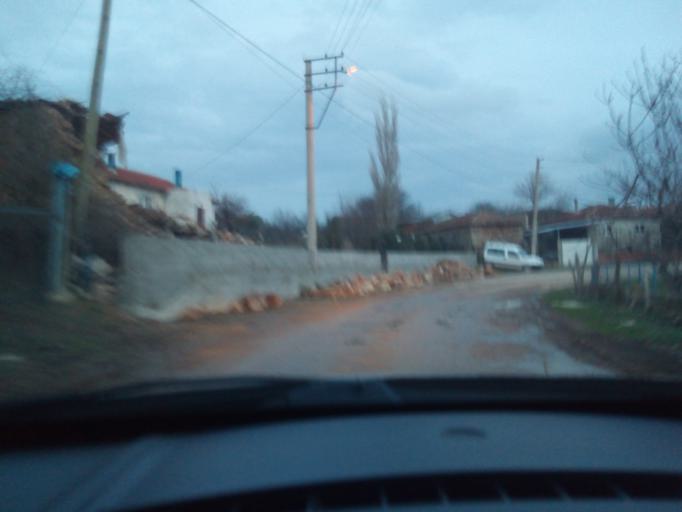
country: TR
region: Balikesir
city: Susurluk
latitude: 39.9170
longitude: 28.0876
